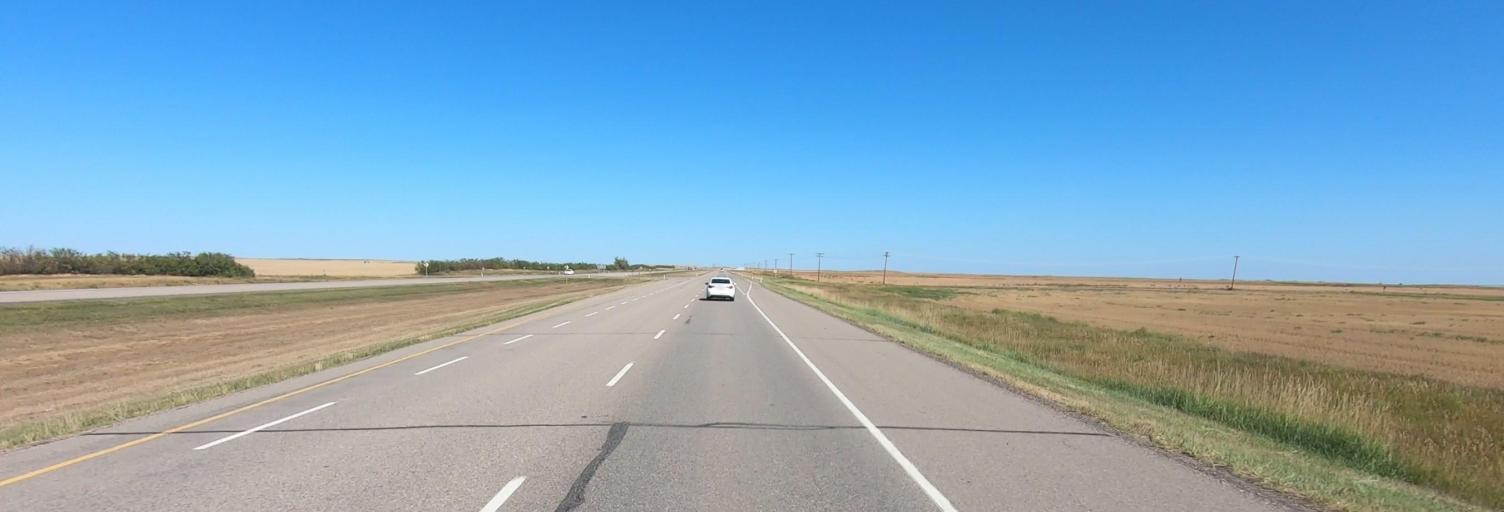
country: CA
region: Alberta
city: Bassano
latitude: 50.8034
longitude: -112.4511
